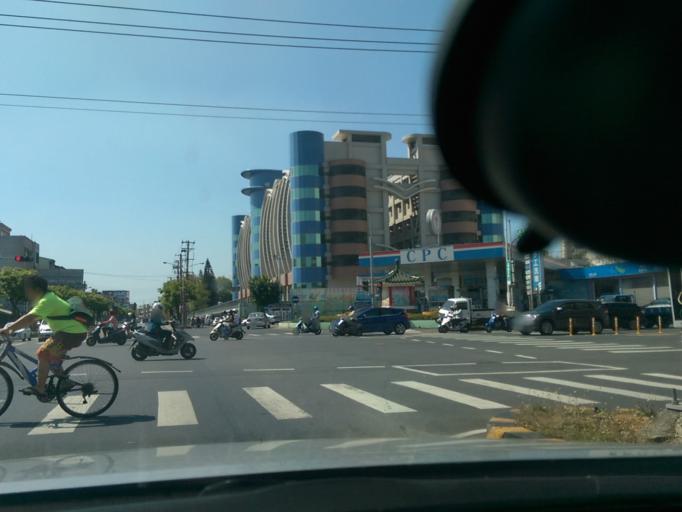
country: TW
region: Taiwan
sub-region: Chiayi
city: Jiayi Shi
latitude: 23.4696
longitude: 120.4543
